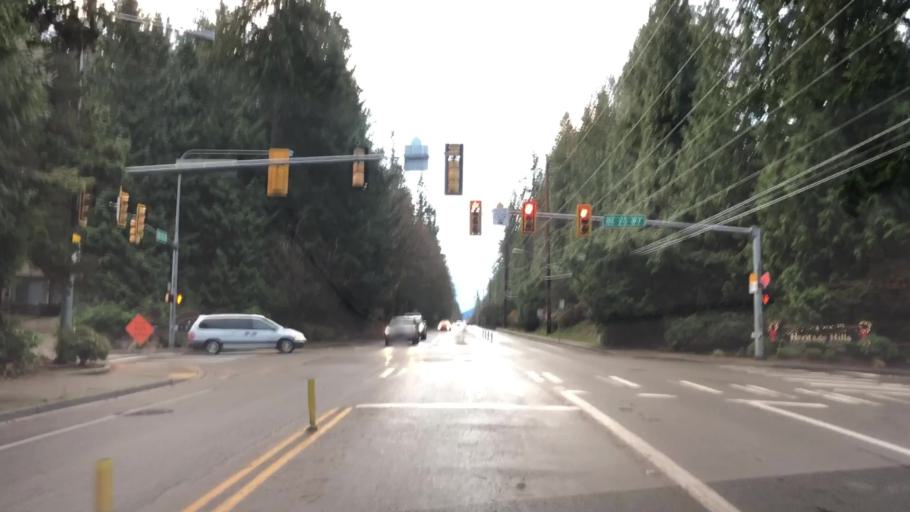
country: US
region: Washington
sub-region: King County
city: City of Sammamish
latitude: 47.6318
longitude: -122.0354
